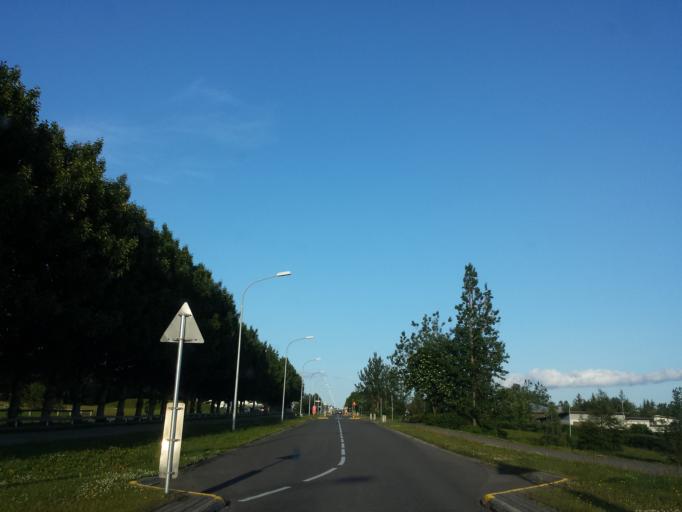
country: IS
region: Capital Region
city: Reykjavik
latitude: 64.1175
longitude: -21.8060
